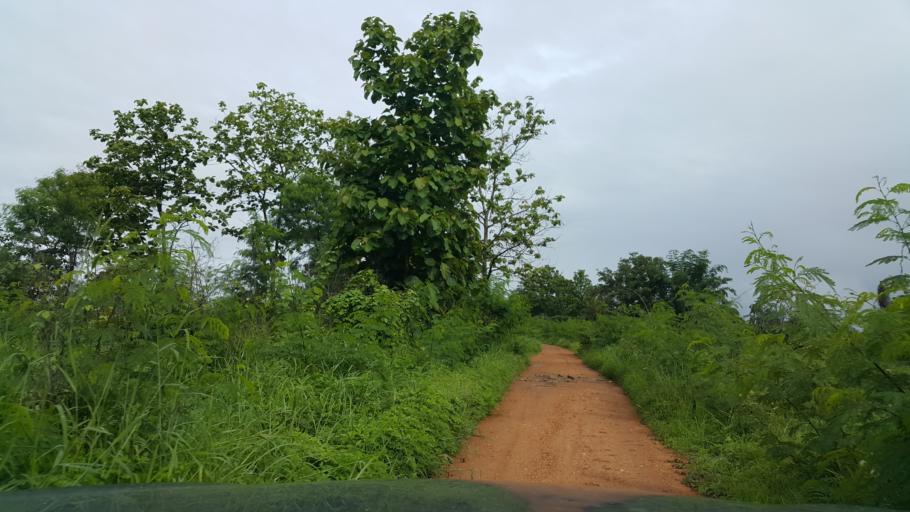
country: TH
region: Chiang Mai
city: San Kamphaeng
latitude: 18.7315
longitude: 99.1882
